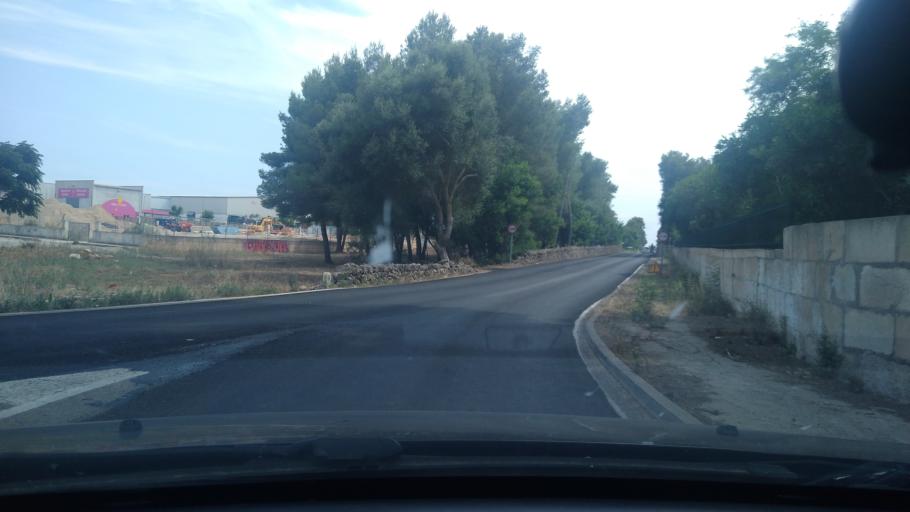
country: ES
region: Balearic Islands
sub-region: Illes Balears
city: Santa Margalida
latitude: 39.7494
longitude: 3.1484
